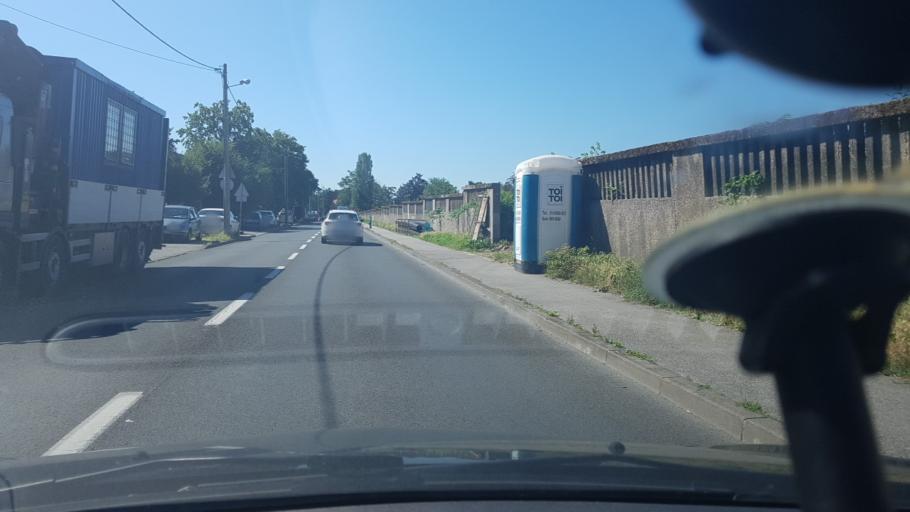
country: HR
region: Grad Zagreb
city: Zagreb
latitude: 45.8203
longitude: 15.9870
